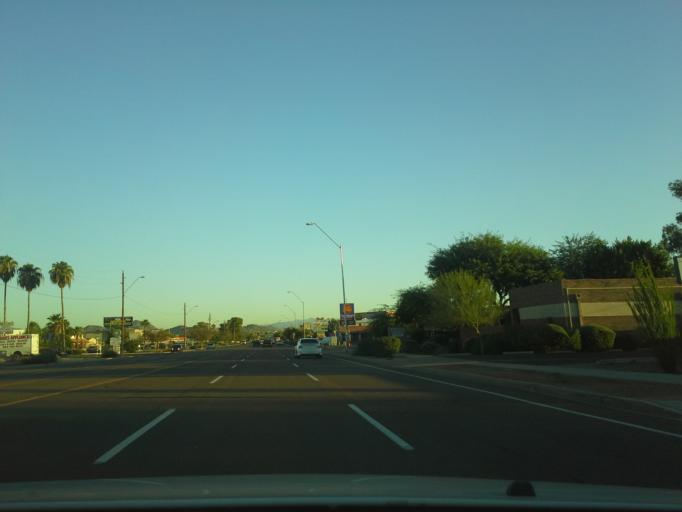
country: US
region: Arizona
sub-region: Maricopa County
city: Paradise Valley
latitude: 33.6220
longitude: -112.0306
